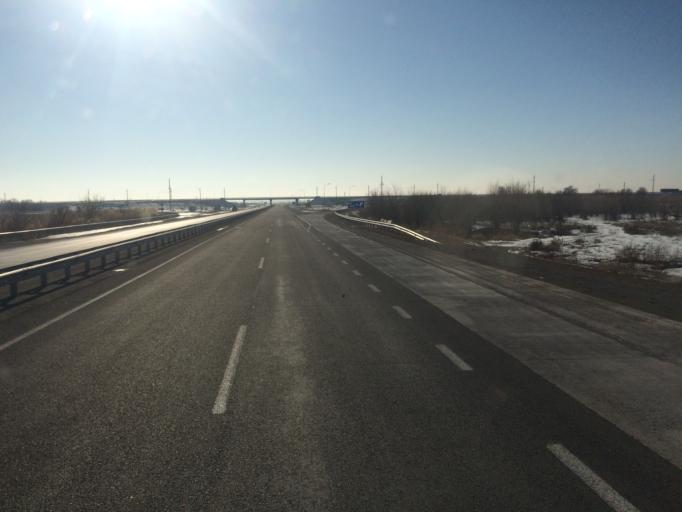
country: KG
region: Chuy
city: Sokuluk
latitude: 43.2797
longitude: 74.2342
